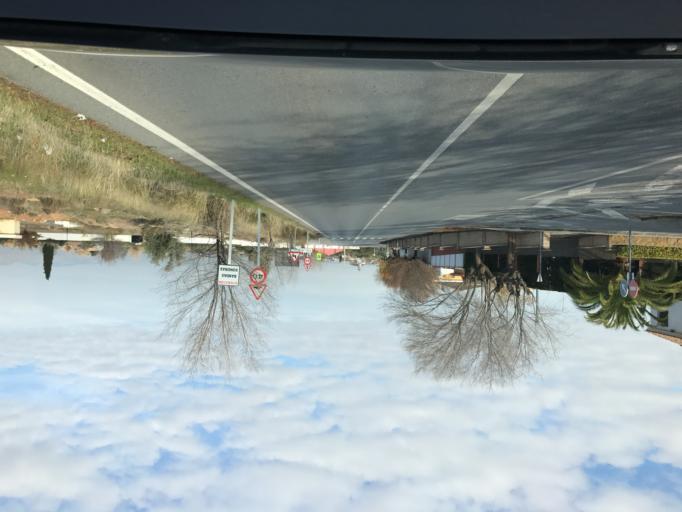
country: ES
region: Andalusia
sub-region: Provincia de Granada
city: Otura
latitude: 37.0886
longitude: -3.6237
